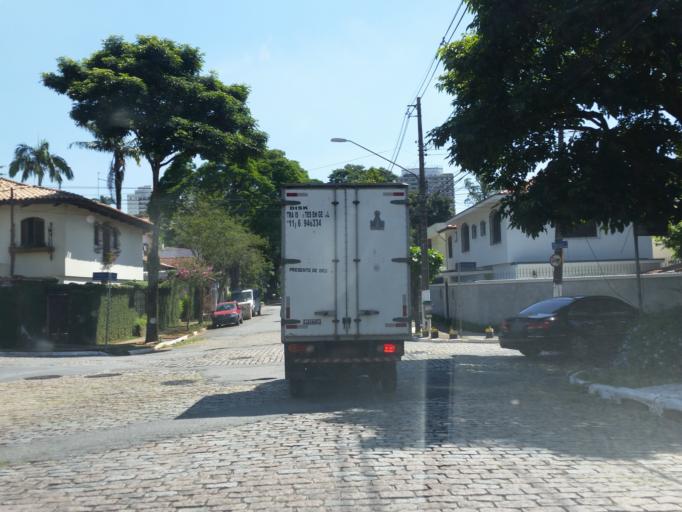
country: BR
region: Sao Paulo
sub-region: Diadema
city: Diadema
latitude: -23.6486
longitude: -46.6965
